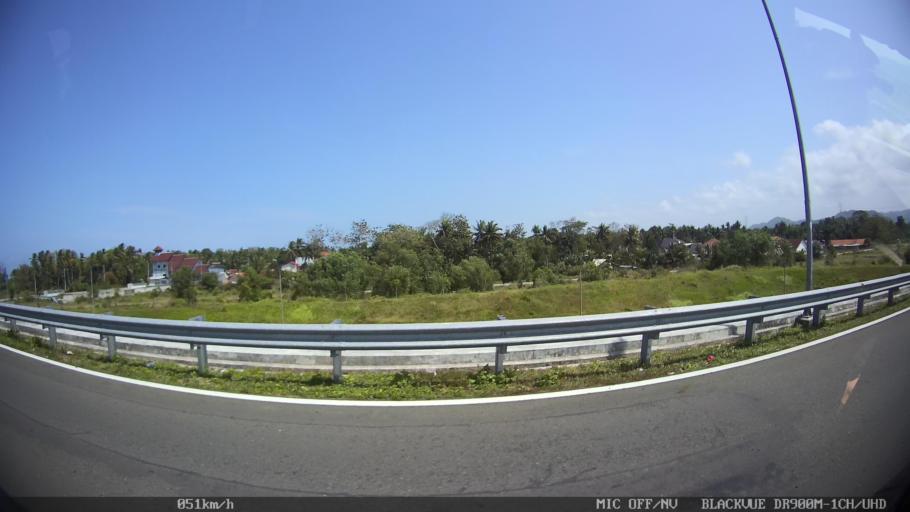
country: ID
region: Daerah Istimewa Yogyakarta
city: Srandakan
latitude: -7.8949
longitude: 110.0571
